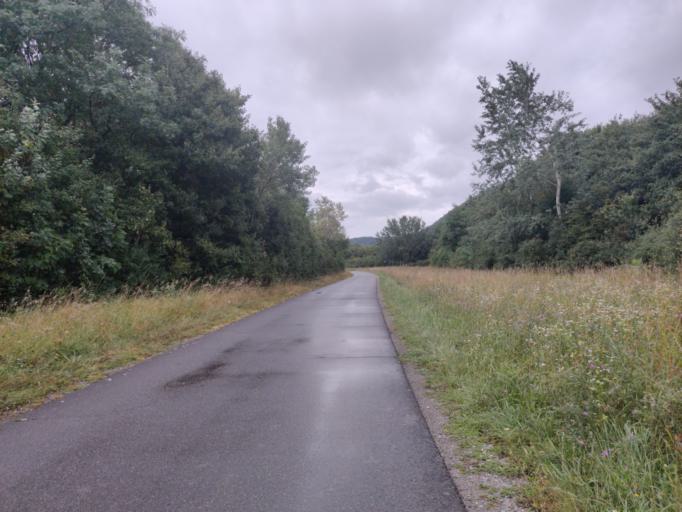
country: AT
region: Lower Austria
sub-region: Politischer Bezirk Korneuburg
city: Langenzersdorf
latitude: 48.2902
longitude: 16.3522
